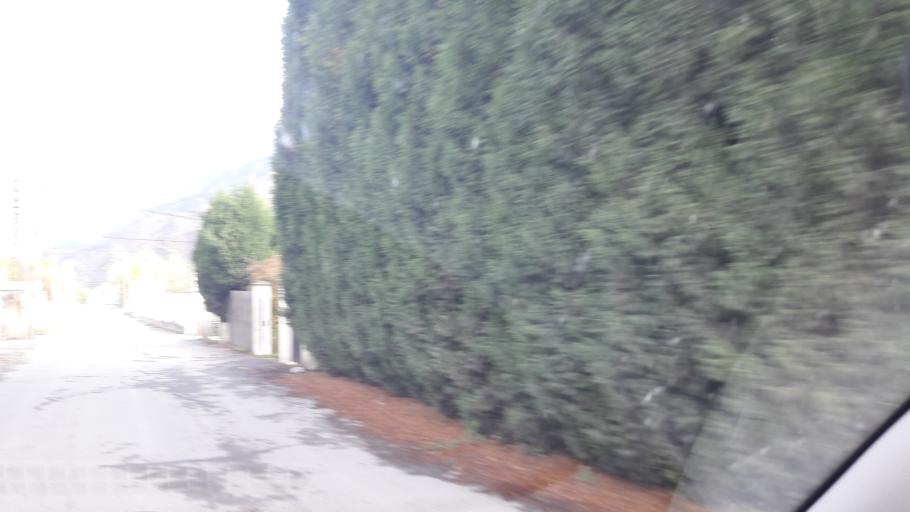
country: FR
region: Rhone-Alpes
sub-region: Departement de la Savoie
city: Saint-Jean-de-Maurienne
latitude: 45.2687
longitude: 6.3513
